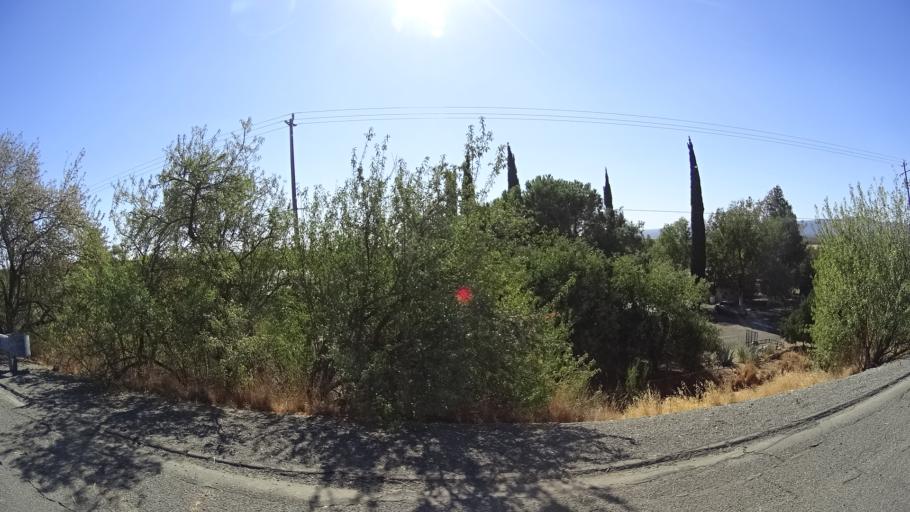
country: US
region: California
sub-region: Yolo County
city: Winters
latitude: 38.5618
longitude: -121.9539
